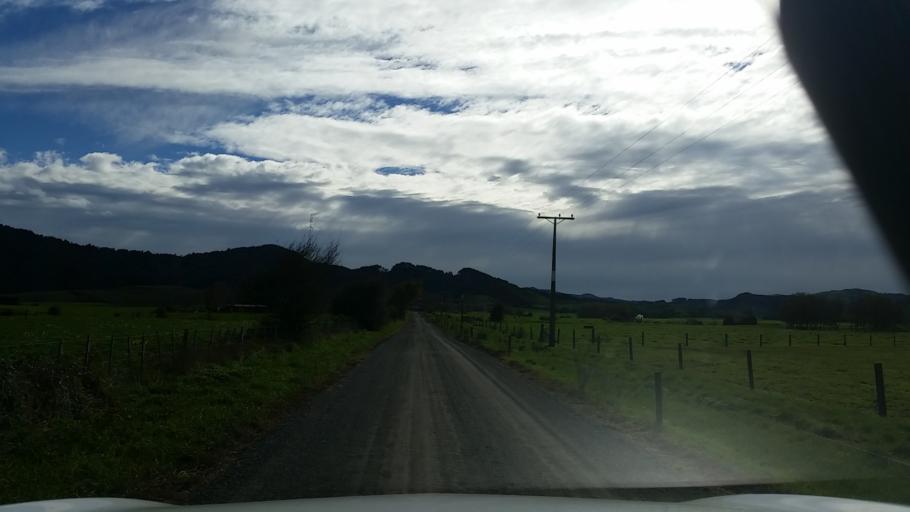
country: NZ
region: Waikato
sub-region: Hauraki District
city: Ngatea
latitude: -37.5131
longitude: 175.4094
